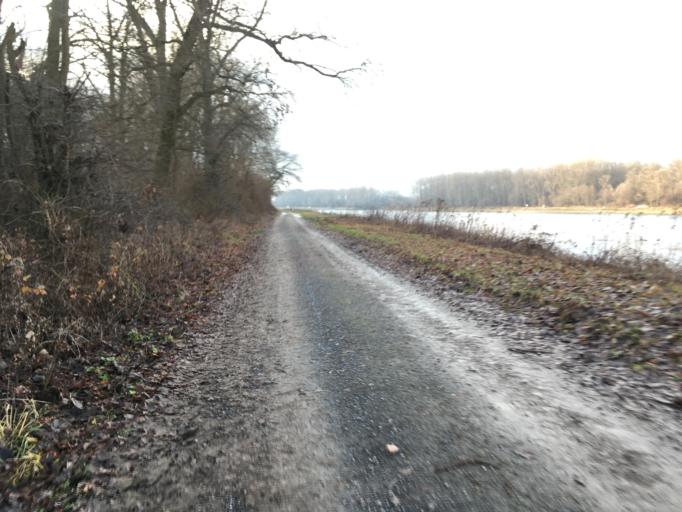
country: DE
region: Rheinland-Pfalz
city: Germersheim
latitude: 49.2462
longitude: 8.4077
